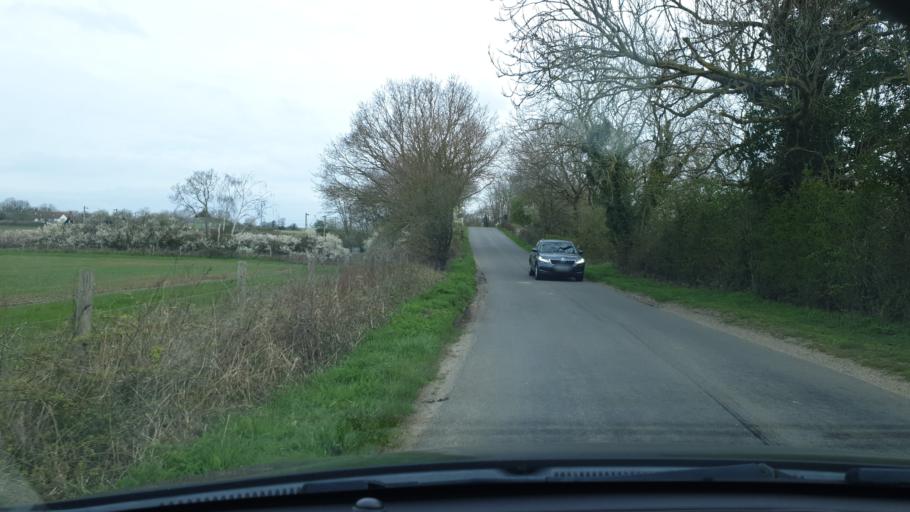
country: GB
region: England
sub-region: Essex
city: Great Bentley
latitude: 51.8518
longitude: 1.0865
